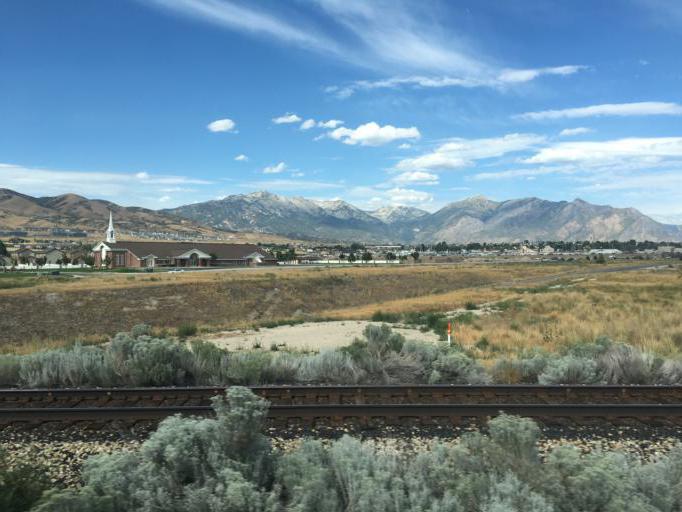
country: US
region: Utah
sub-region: Utah County
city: Lehi
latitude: 40.4120
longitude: -111.8814
